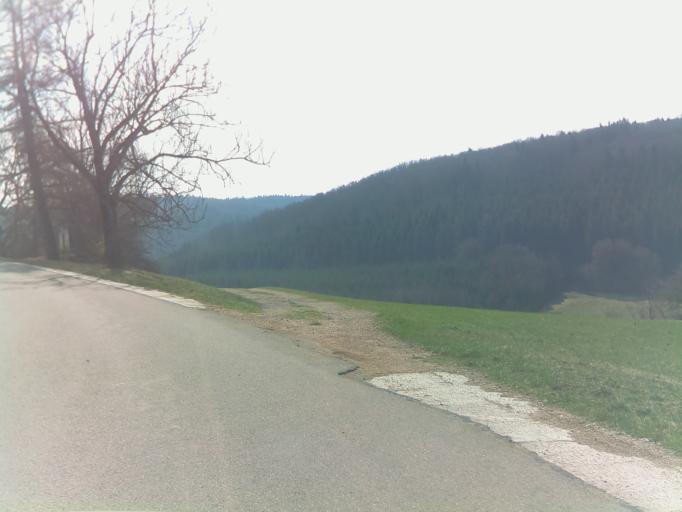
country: DE
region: Baden-Wuerttemberg
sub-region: Tuebingen Region
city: Bad Urach
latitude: 48.4501
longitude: 9.4064
